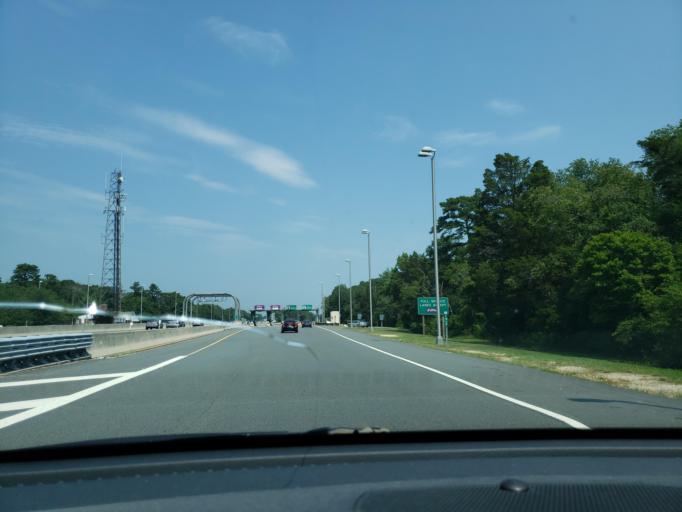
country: US
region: New Jersey
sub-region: Cape May County
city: Sea Isle City
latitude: 39.1925
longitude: -74.7109
